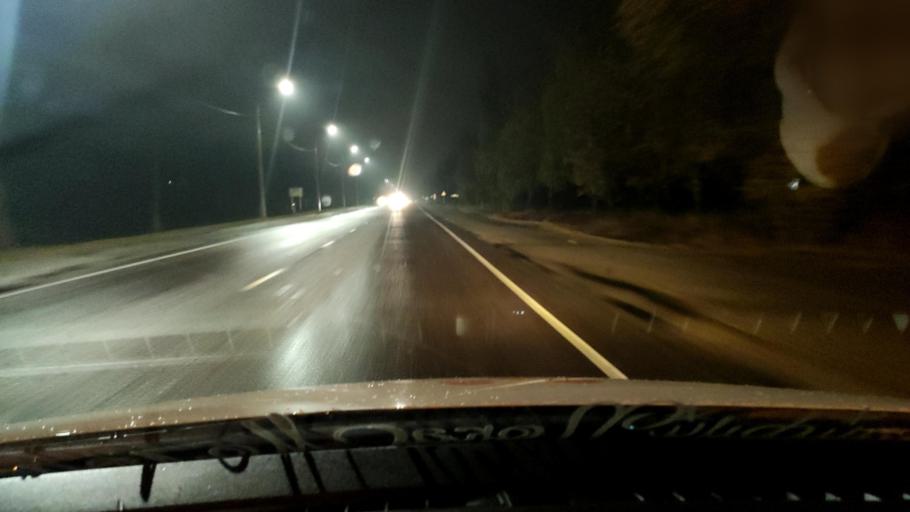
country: RU
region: Voronezj
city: Semiluki
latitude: 51.7067
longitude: 39.0217
